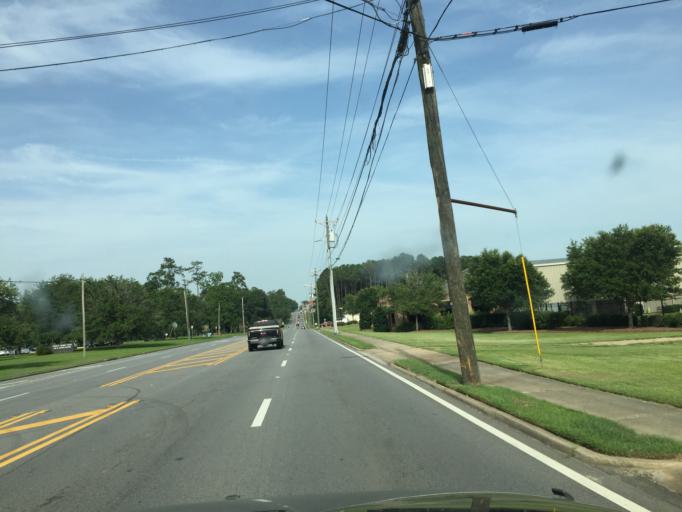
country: US
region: Georgia
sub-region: Thomas County
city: Thomasville
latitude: 30.8354
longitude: -83.9645
